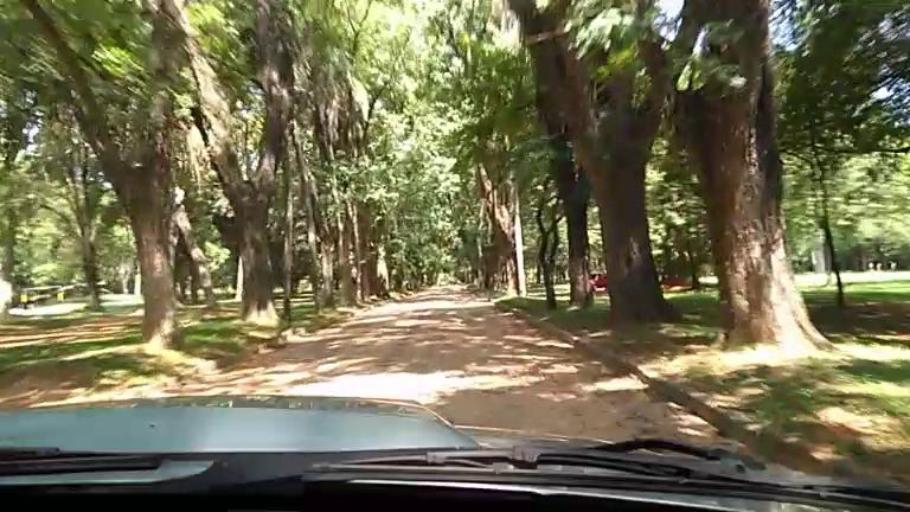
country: PY
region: Asuncion
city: Asuncion
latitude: -25.2473
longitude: -57.5758
